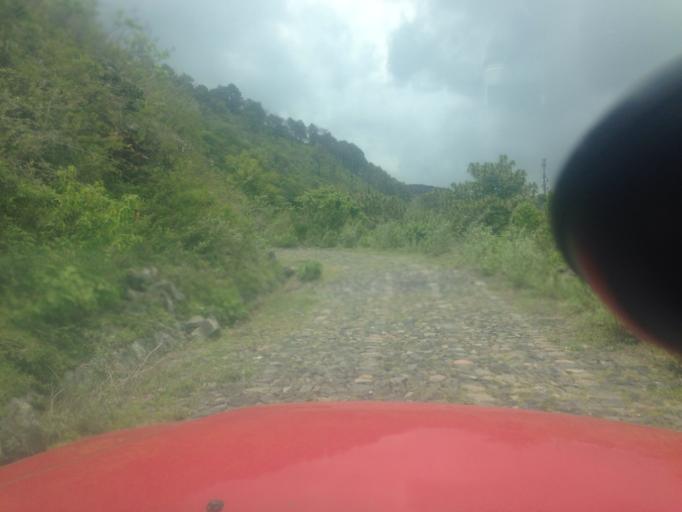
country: MX
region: Nayarit
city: Jala
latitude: 21.1287
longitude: -104.5007
